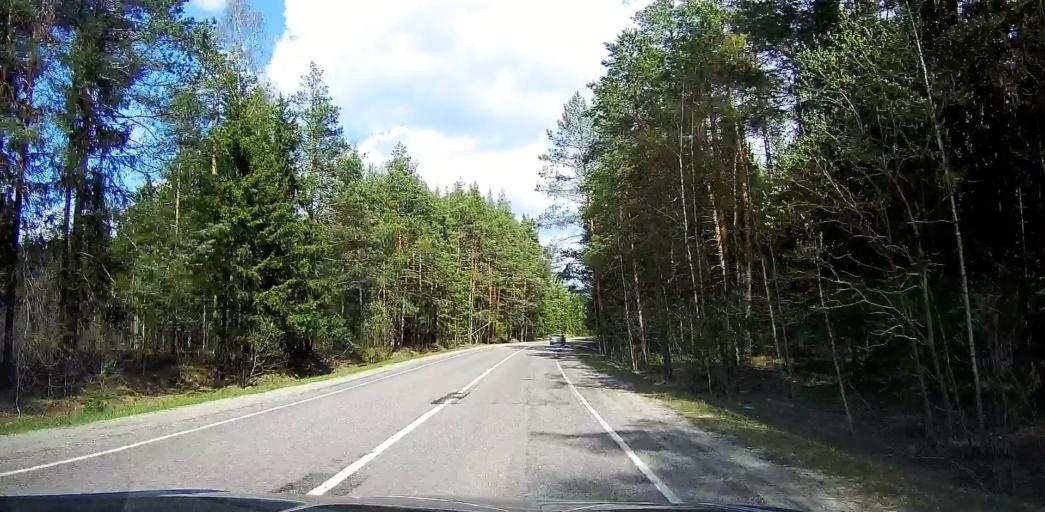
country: RU
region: Moskovskaya
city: Davydovo
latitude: 55.5646
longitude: 38.8165
